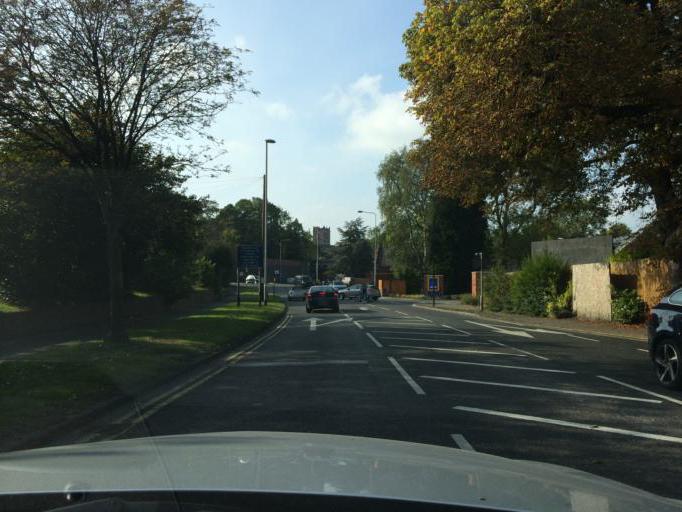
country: GB
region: England
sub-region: Cheshire East
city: Knutsford
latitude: 53.3017
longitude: -2.3687
